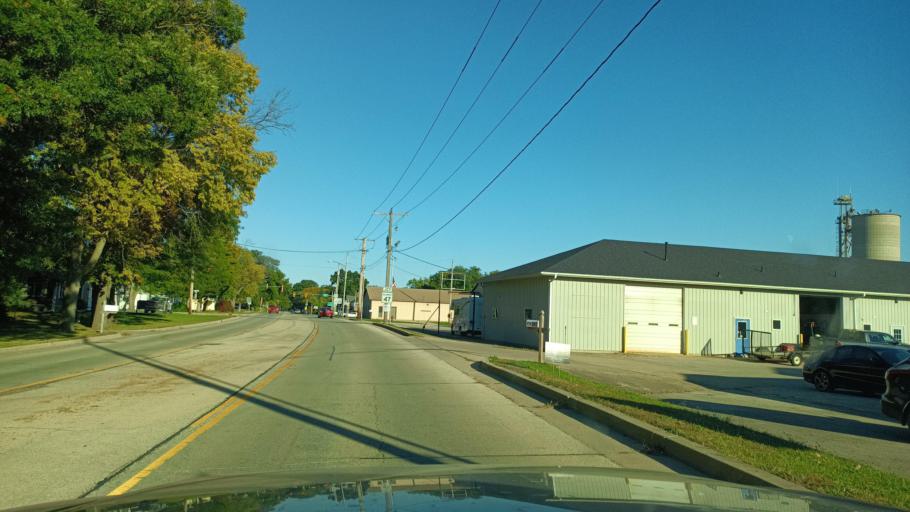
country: US
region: Illinois
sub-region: Champaign County
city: Mahomet
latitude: 40.1919
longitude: -88.4102
